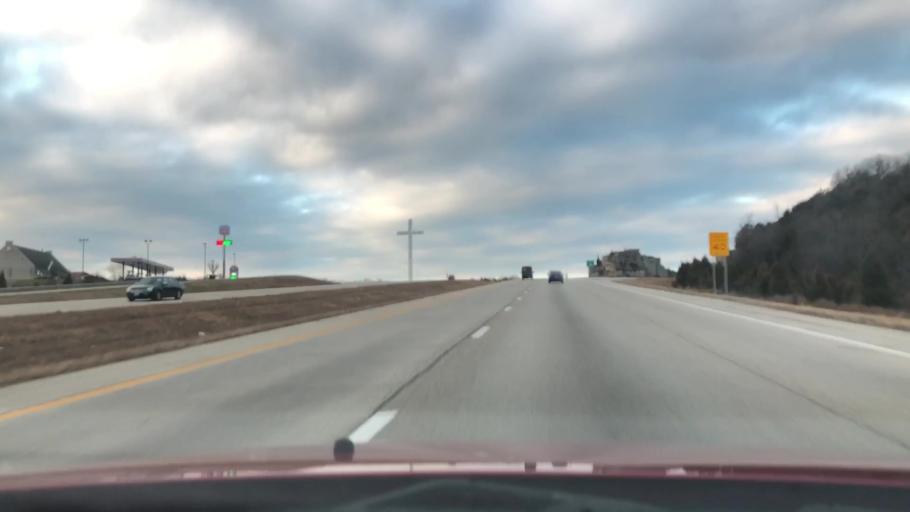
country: US
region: Missouri
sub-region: Taney County
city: Merriam Woods
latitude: 36.7446
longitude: -93.2223
